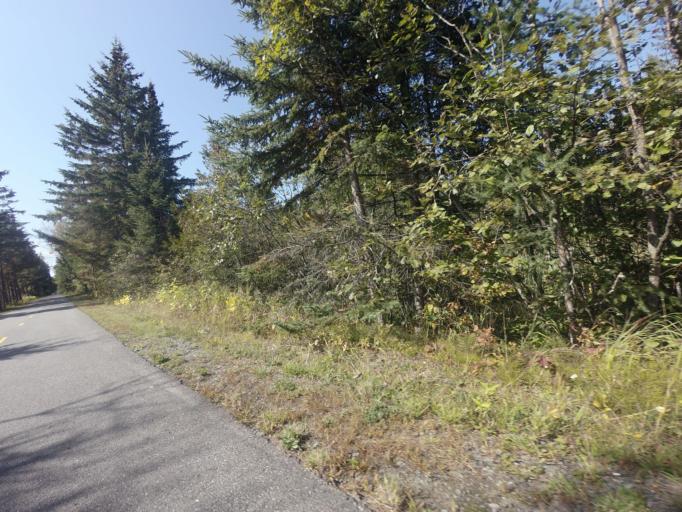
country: CA
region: Quebec
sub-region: Laurentides
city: Mont-Tremblant
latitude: 46.1285
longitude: -74.5600
